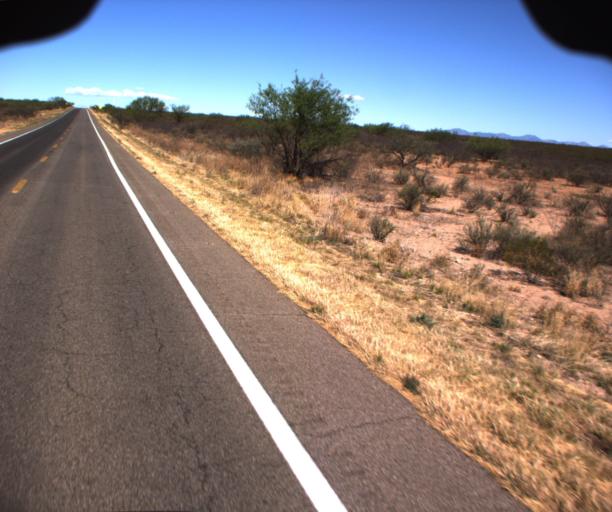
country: US
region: Arizona
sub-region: Cochise County
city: Sierra Vista Southeast
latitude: 31.5494
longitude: -110.1765
